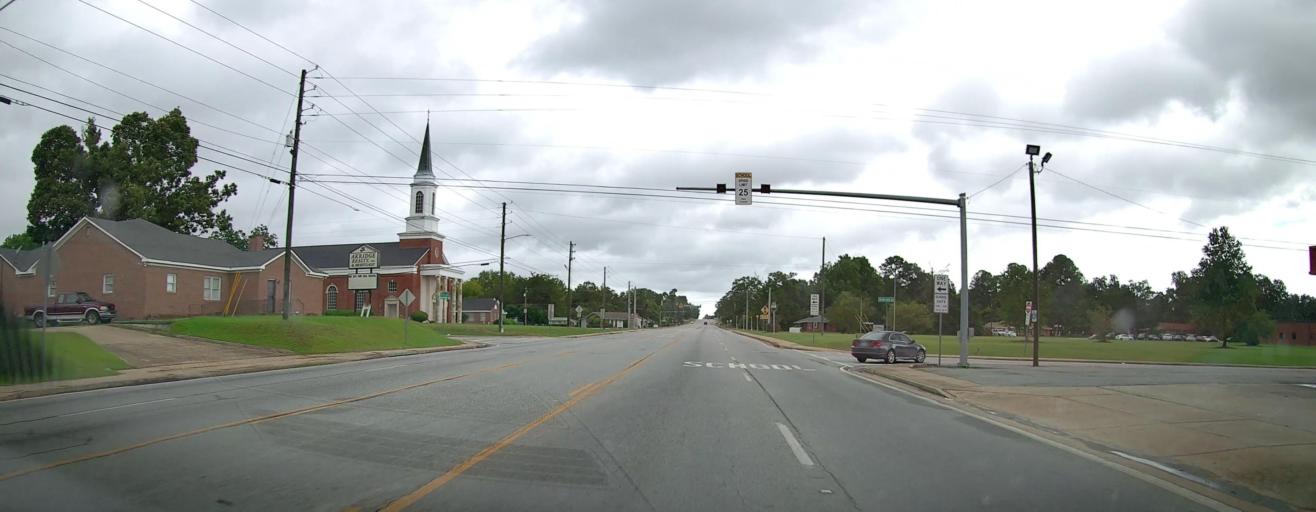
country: US
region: Georgia
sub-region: Bibb County
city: Macon
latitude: 32.7878
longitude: -83.7077
